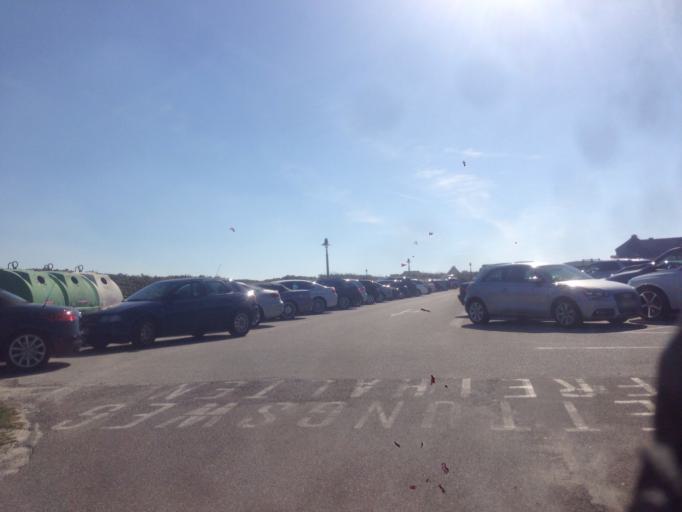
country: DE
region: Schleswig-Holstein
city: Westerland
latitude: 54.9627
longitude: 8.3344
